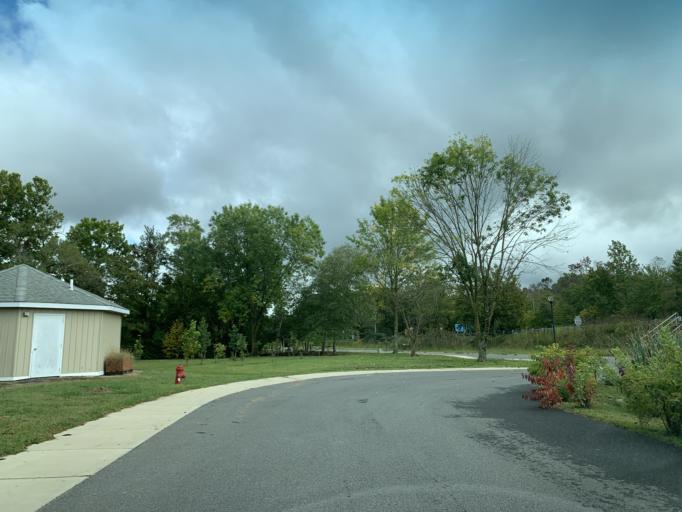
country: US
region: Maryland
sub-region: Caroline County
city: Denton
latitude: 38.8881
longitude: -75.8370
